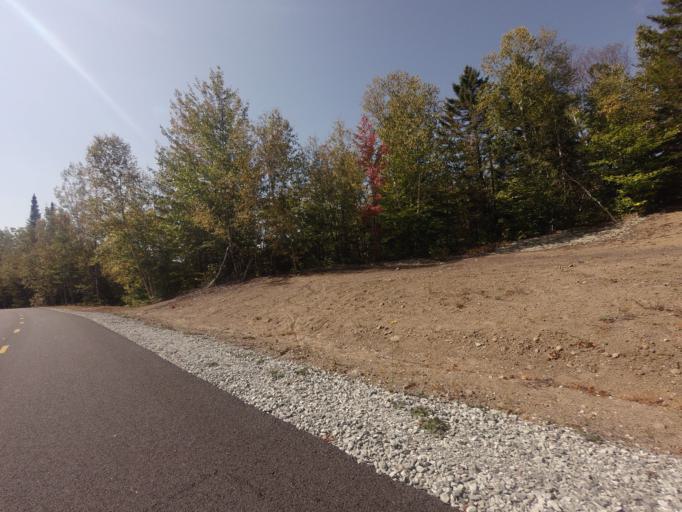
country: CA
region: Quebec
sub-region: Laurentides
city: Mont-Tremblant
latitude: 46.1329
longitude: -74.4920
